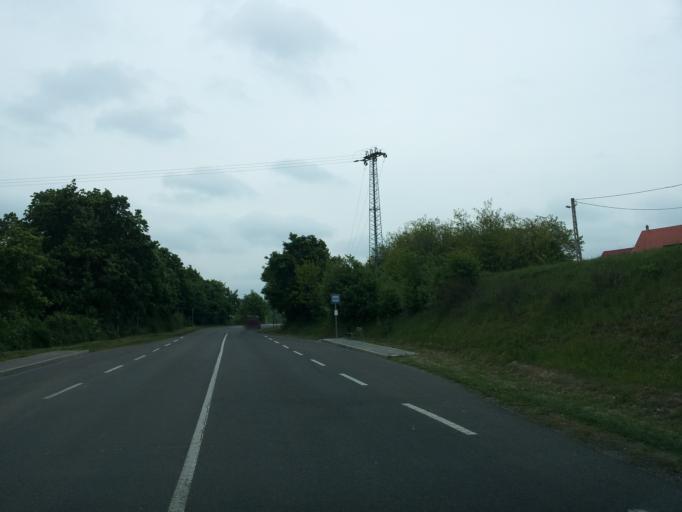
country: HU
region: Baranya
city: Hosszuheteny
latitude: 46.1449
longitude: 18.3495
